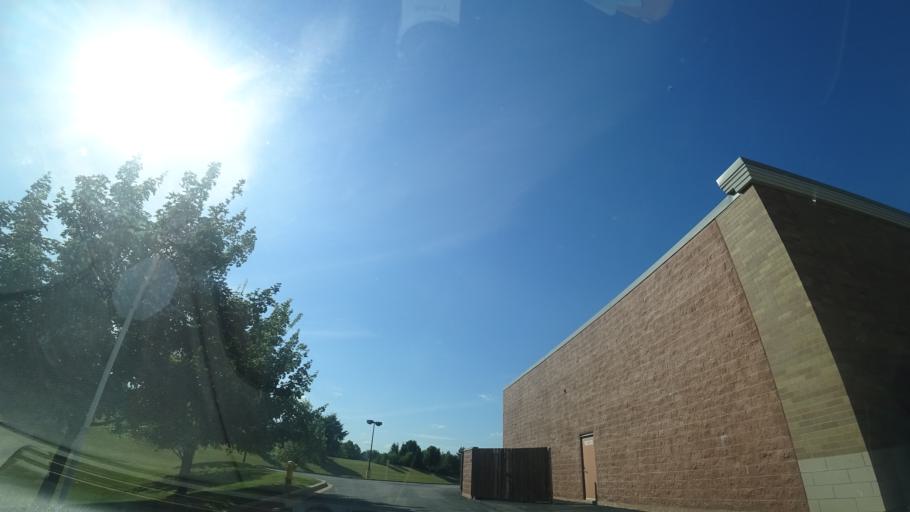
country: US
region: Illinois
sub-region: Will County
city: Mokena
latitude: 41.5617
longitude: -87.8929
